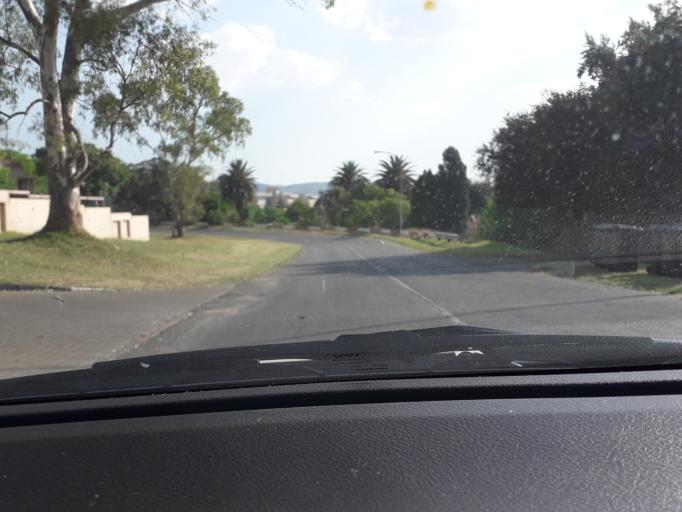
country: ZA
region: Gauteng
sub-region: City of Johannesburg Metropolitan Municipality
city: Modderfontein
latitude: -26.1245
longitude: 28.1320
